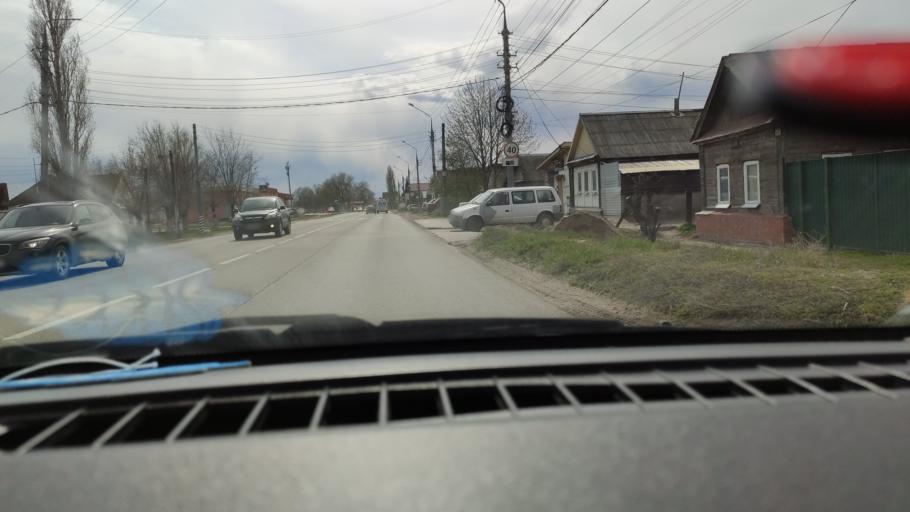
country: RU
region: Saratov
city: Privolzhskiy
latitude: 51.4249
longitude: 46.0461
